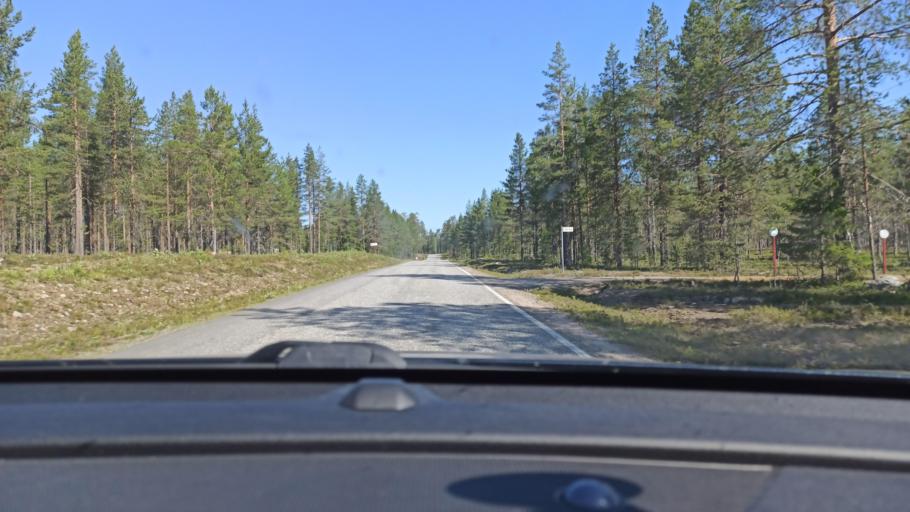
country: FI
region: Lapland
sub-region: Tunturi-Lappi
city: Kolari
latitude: 67.6558
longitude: 24.1642
